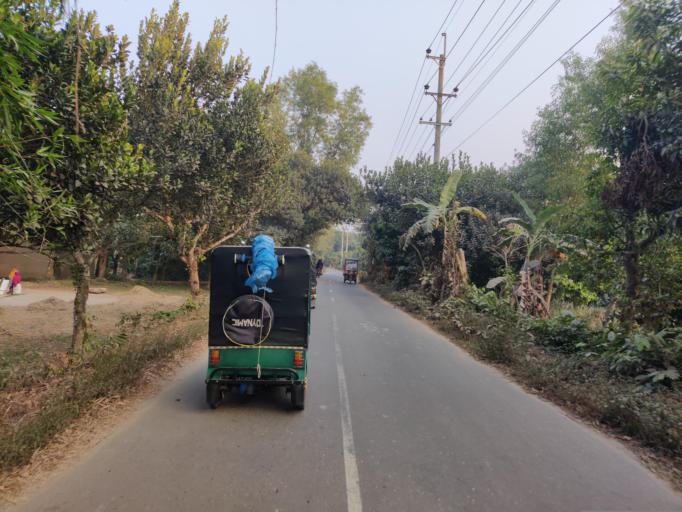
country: BD
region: Dhaka
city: Bajitpur
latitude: 24.1564
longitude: 90.7694
